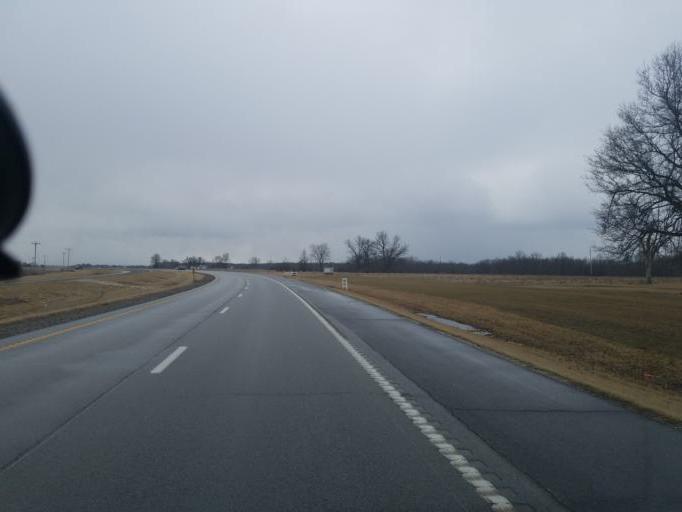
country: US
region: Missouri
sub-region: Macon County
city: Macon
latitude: 39.8470
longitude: -92.4811
